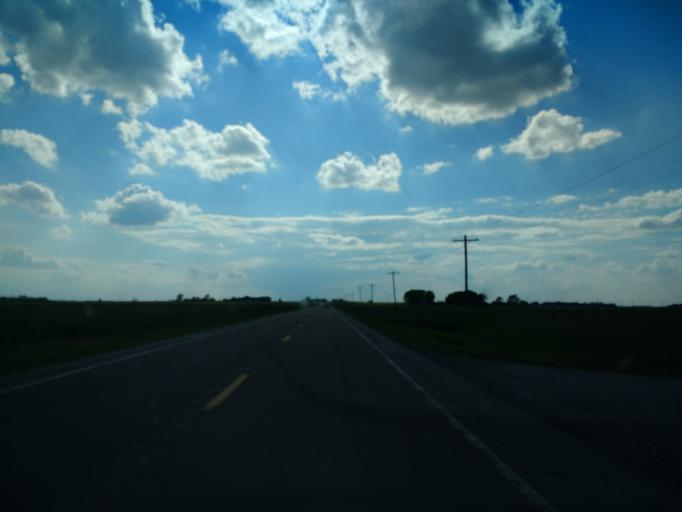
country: US
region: Iowa
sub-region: Clay County
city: Spencer
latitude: 43.1838
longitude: -95.2222
